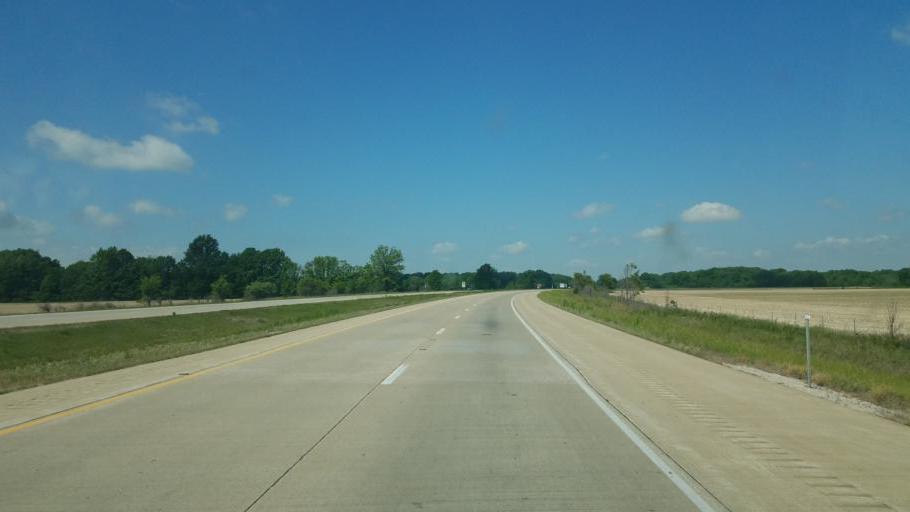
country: US
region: Illinois
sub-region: Clark County
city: Marshall
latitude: 39.4221
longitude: -87.6304
